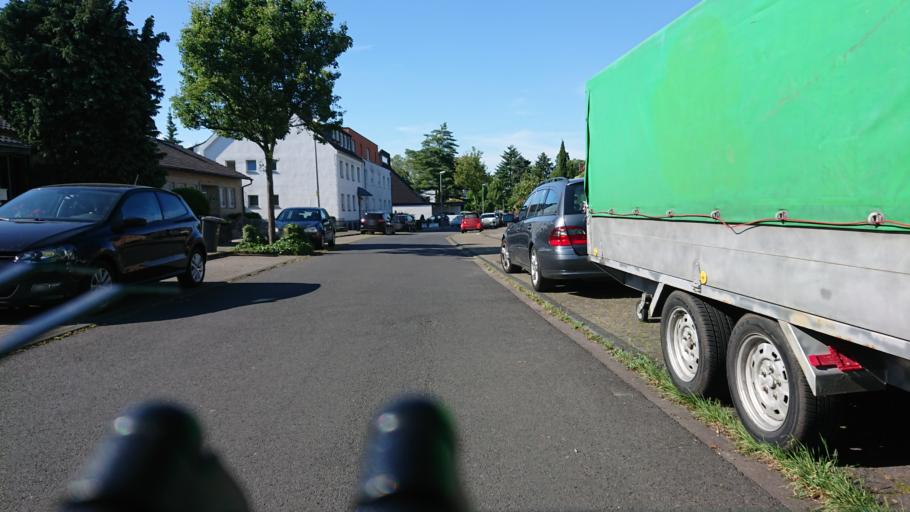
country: DE
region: North Rhine-Westphalia
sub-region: Regierungsbezirk Koln
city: Frechen
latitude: 50.9331
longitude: 6.8518
